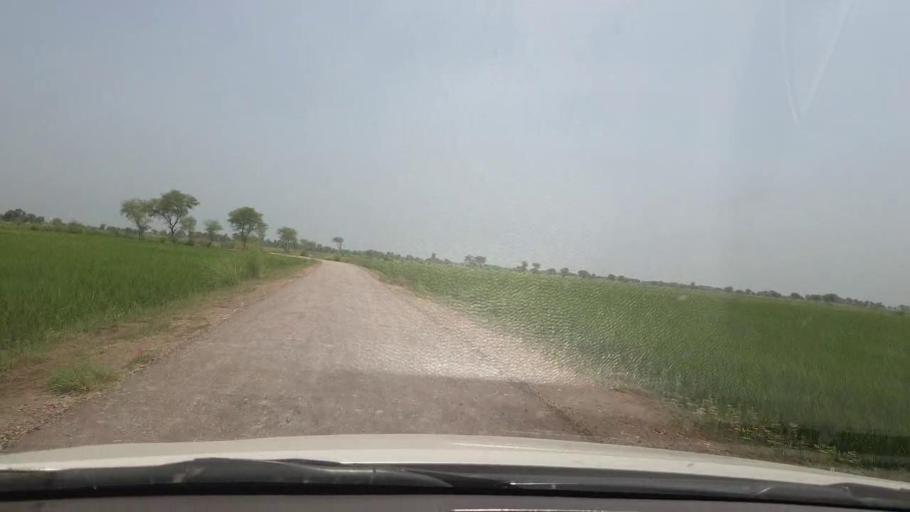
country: PK
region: Sindh
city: Shikarpur
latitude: 28.0940
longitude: 68.6297
